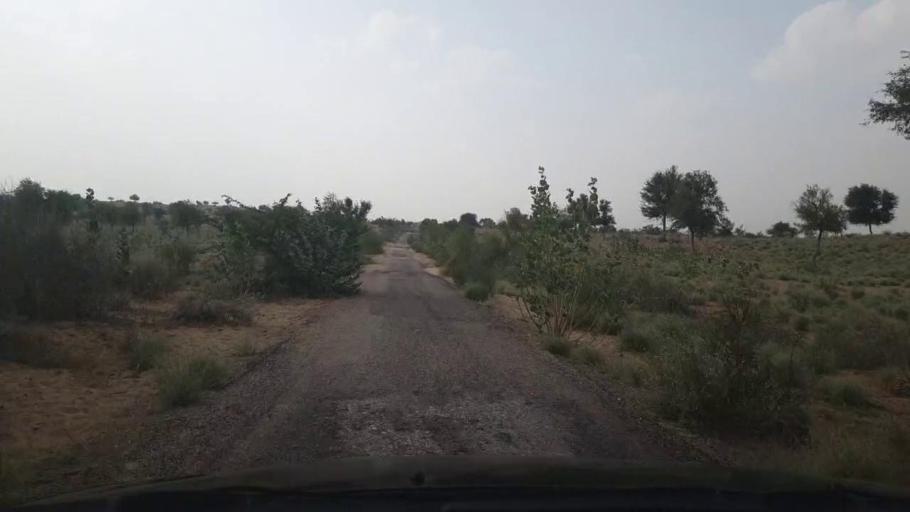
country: PK
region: Sindh
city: Islamkot
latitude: 24.9705
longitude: 70.5925
